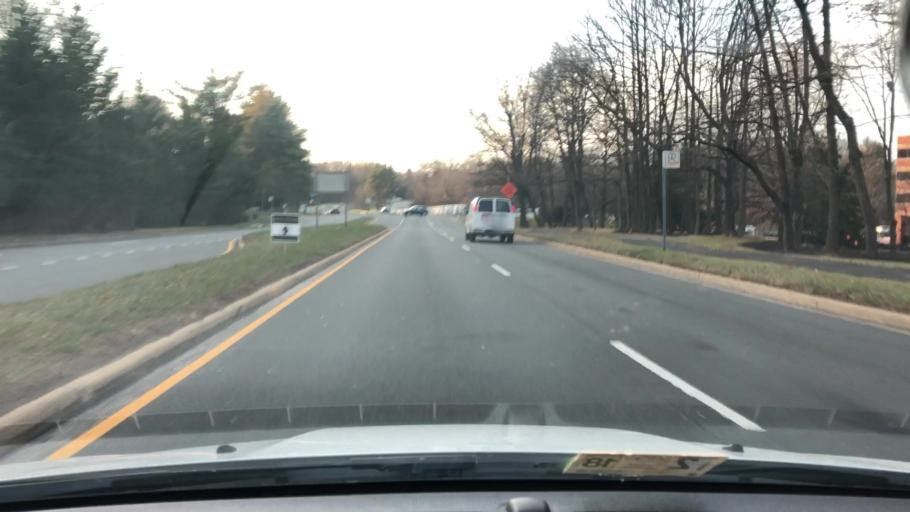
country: US
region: Virginia
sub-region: Fairfax County
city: Reston
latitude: 38.9452
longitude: -77.3416
